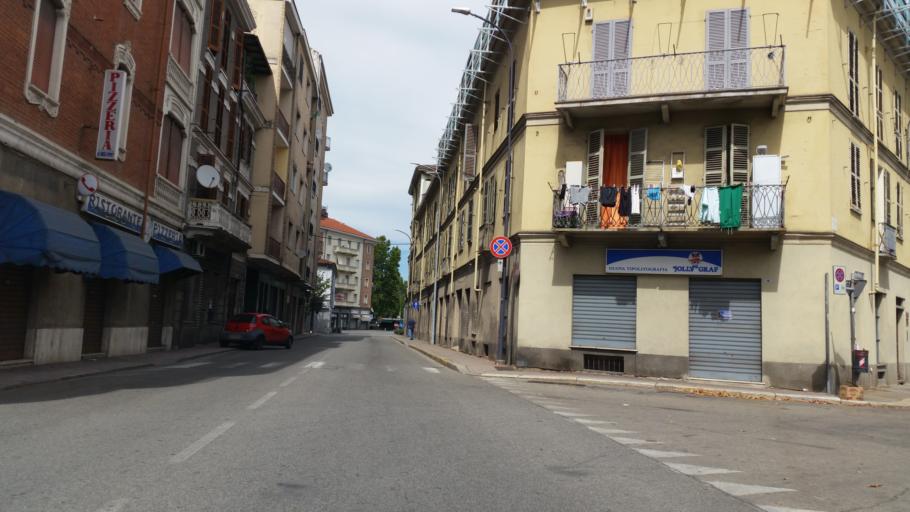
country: IT
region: Piedmont
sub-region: Provincia di Asti
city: Asti
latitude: 44.8952
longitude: 8.2066
